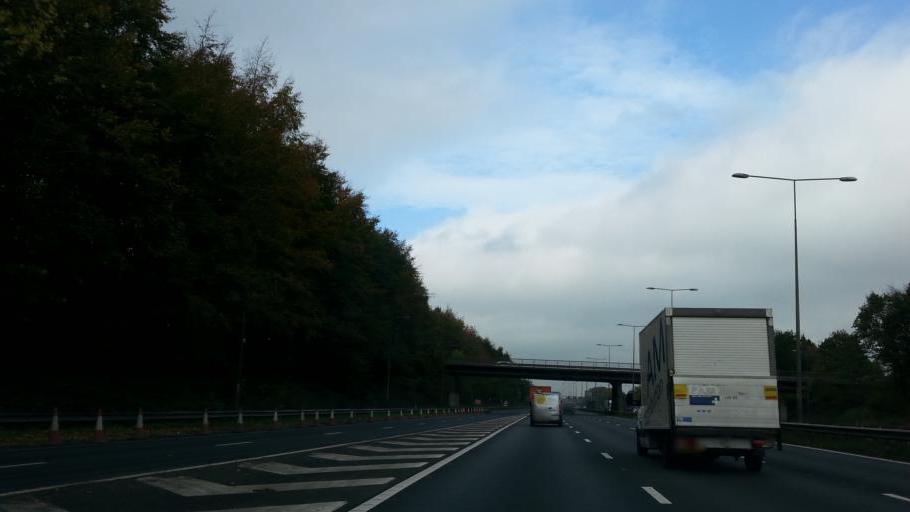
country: GB
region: England
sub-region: Staffordshire
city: Essington
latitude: 52.6459
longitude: -2.0578
